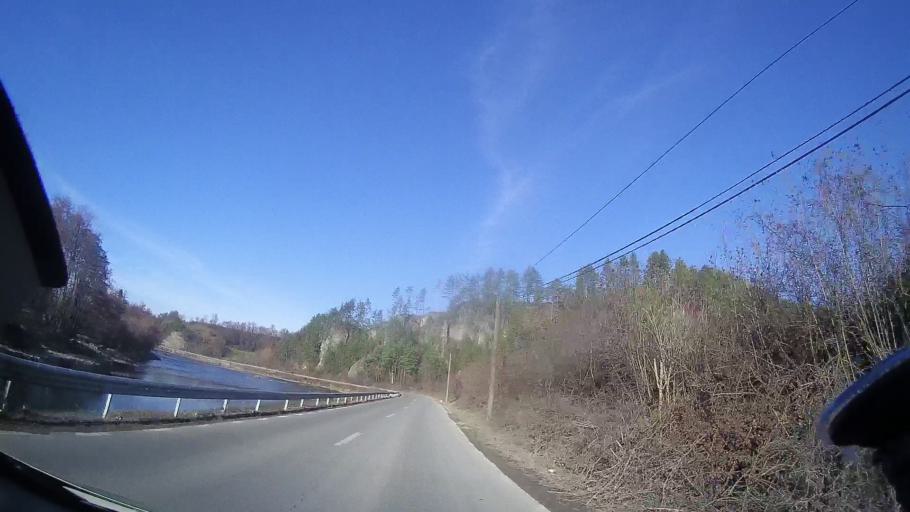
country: RO
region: Bihor
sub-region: Comuna Bratca
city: Bratca
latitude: 46.9224
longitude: 22.6176
